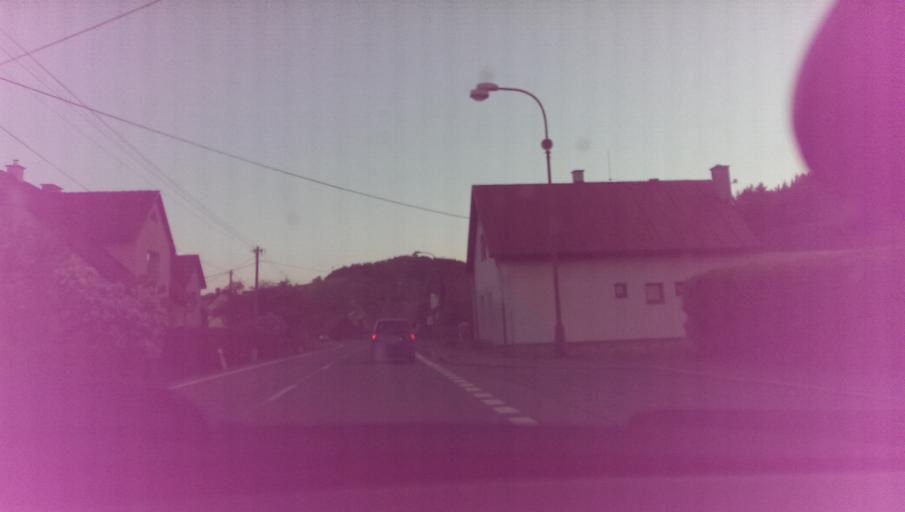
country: CZ
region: Zlin
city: Valasska Polanka
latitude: 49.2912
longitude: 17.9999
